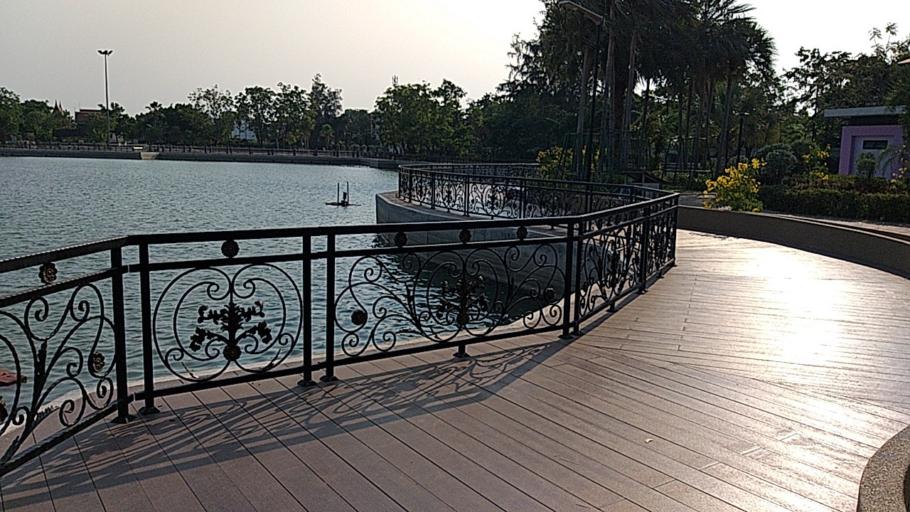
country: TH
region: Bangkok
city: Don Mueang
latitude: 13.9325
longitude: 100.5520
